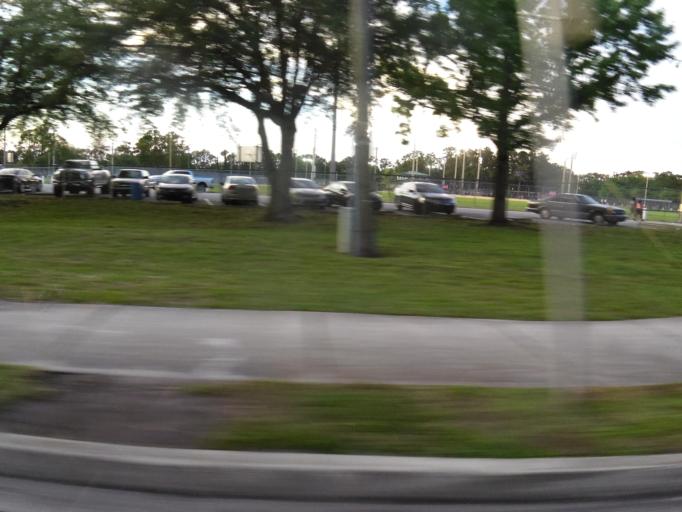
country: US
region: Florida
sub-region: Duval County
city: Jacksonville
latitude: 30.2701
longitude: -81.5932
